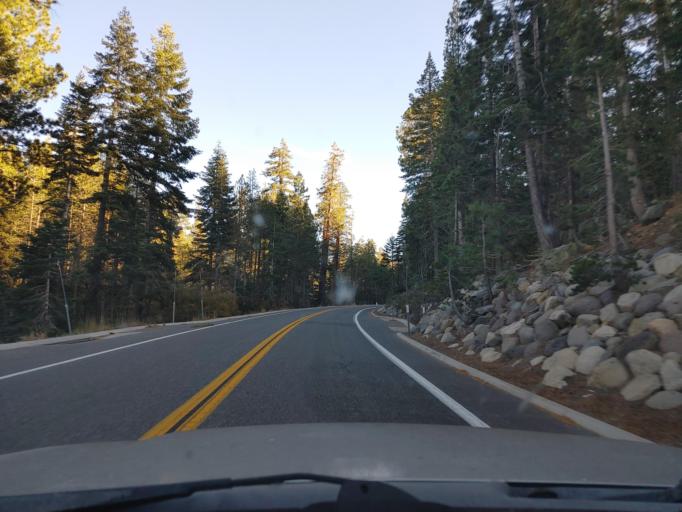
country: US
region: California
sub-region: Placer County
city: Tahoma
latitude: 38.9821
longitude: -120.1056
